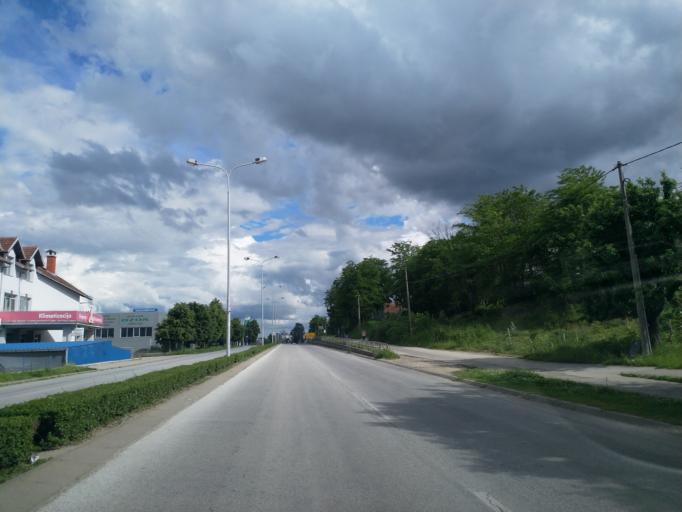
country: RS
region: Central Serbia
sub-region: Pomoravski Okrug
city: Jagodina
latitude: 43.9654
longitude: 21.2766
